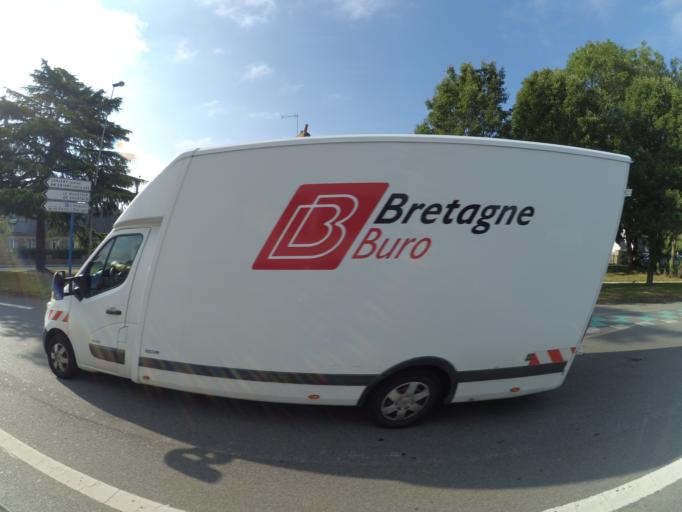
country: FR
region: Brittany
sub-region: Departement du Morbihan
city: Lorient
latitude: 47.7521
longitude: -3.3789
